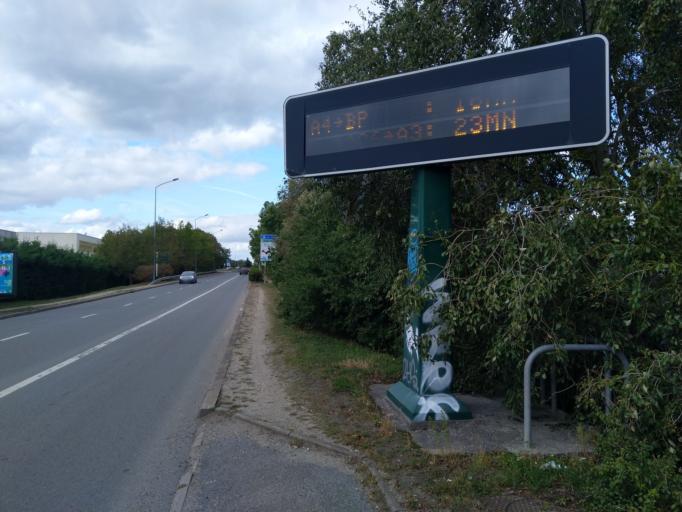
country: FR
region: Ile-de-France
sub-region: Departement de Seine-et-Marne
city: Champs-sur-Marne
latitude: 48.8323
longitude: 2.5840
